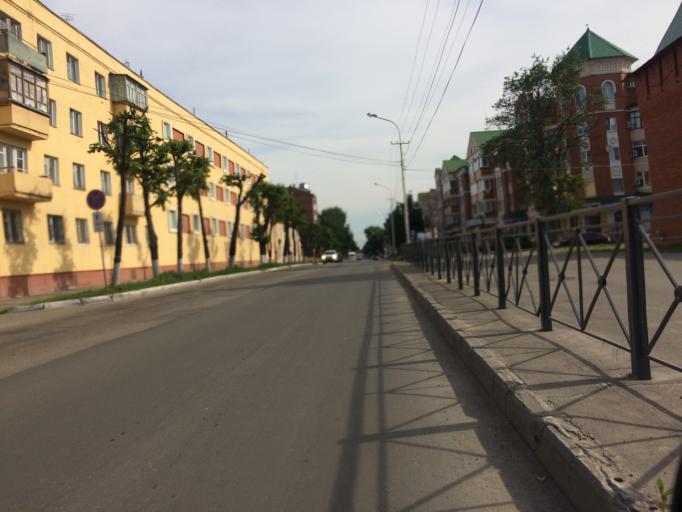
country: RU
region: Mariy-El
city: Yoshkar-Ola
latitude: 56.6377
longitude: 47.8997
